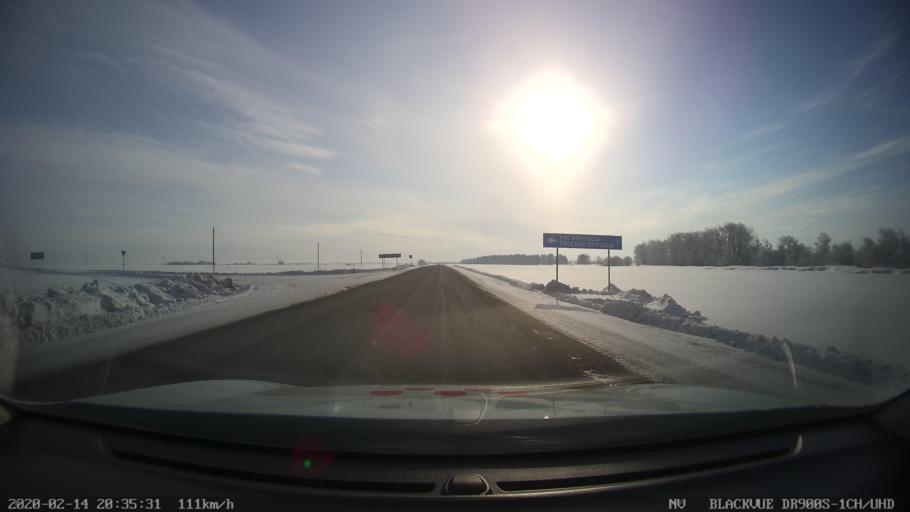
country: RU
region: Tatarstan
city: Kuybyshevskiy Zaton
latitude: 55.3813
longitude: 48.9851
